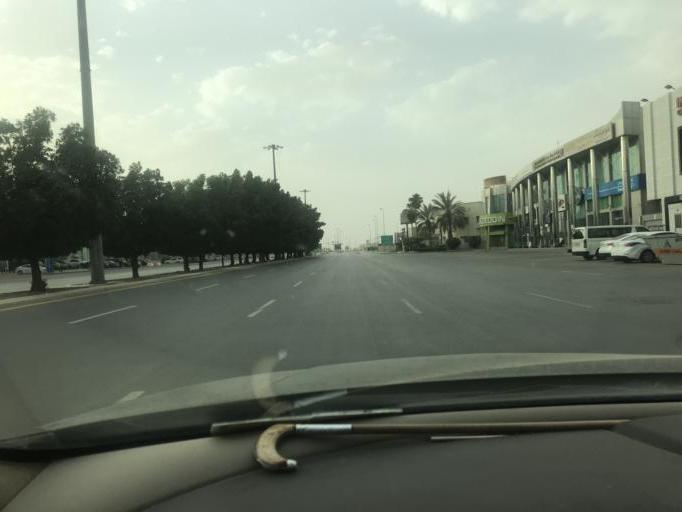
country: SA
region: Ar Riyad
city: Riyadh
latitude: 24.7953
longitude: 46.6558
